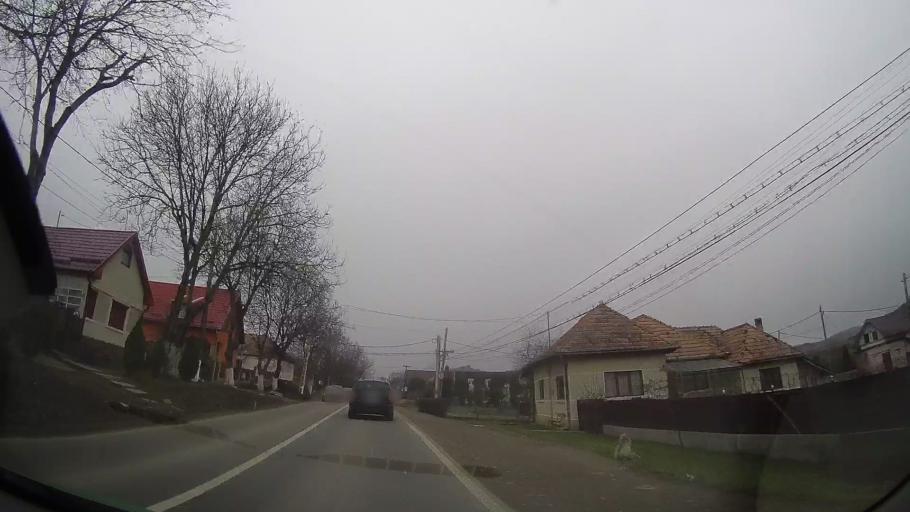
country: RO
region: Mures
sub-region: Comuna Ceausu de Campie
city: Ceausu de Campie
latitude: 46.6072
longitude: 24.5296
